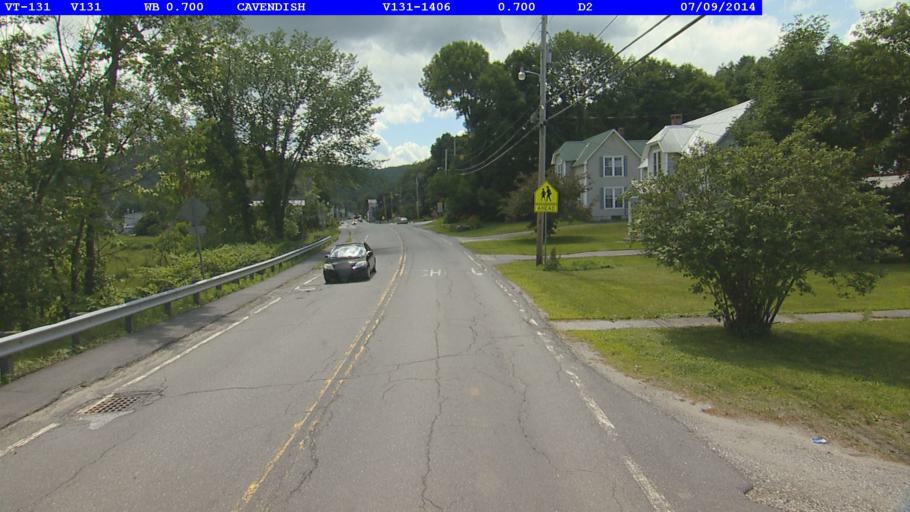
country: US
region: Vermont
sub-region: Windsor County
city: Chester
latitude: 43.3847
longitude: -72.6349
